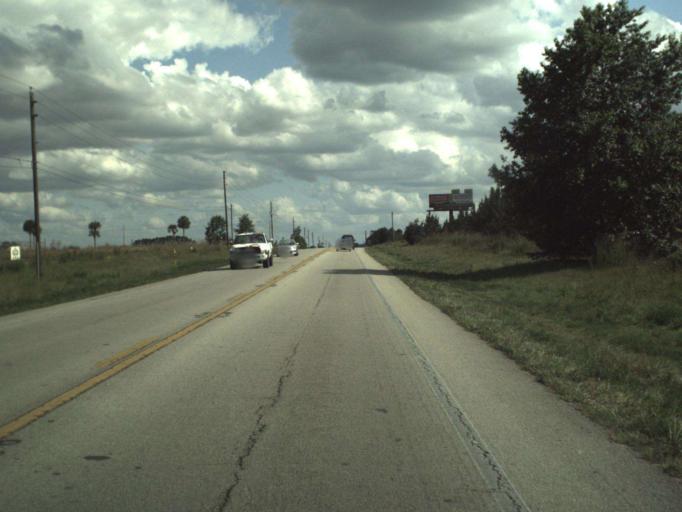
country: US
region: Florida
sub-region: Marion County
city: Silver Springs Shores
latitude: 29.1108
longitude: -82.0536
